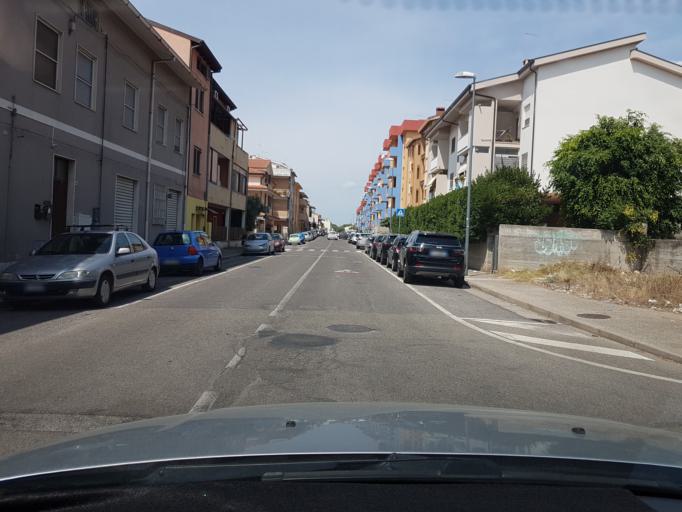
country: IT
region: Sardinia
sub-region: Provincia di Oristano
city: Oristano
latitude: 39.9092
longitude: 8.6003
